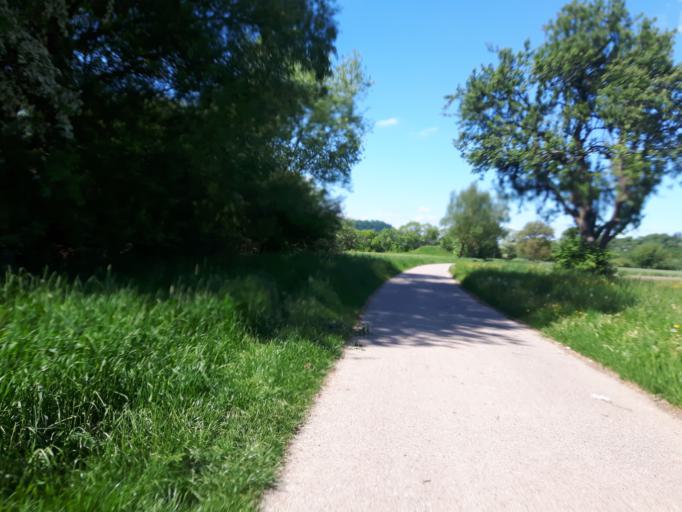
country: DE
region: Baden-Wuerttemberg
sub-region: Regierungsbezirk Stuttgart
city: Offenau
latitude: 49.2530
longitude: 9.1566
